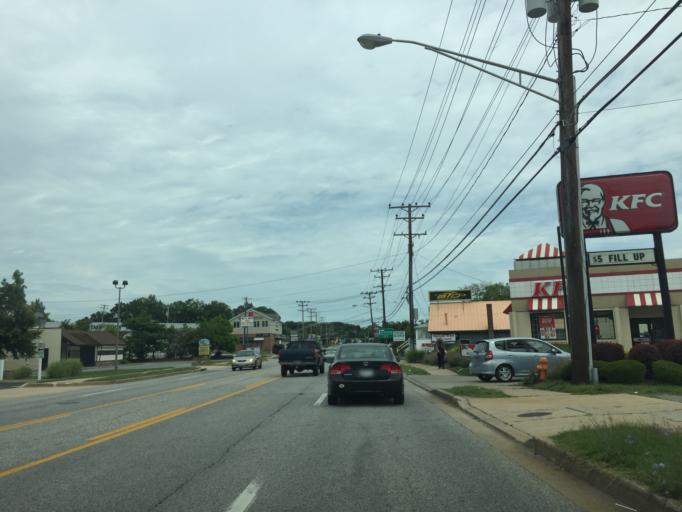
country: US
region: Maryland
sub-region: Baltimore County
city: Carney
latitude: 39.3980
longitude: -76.5397
